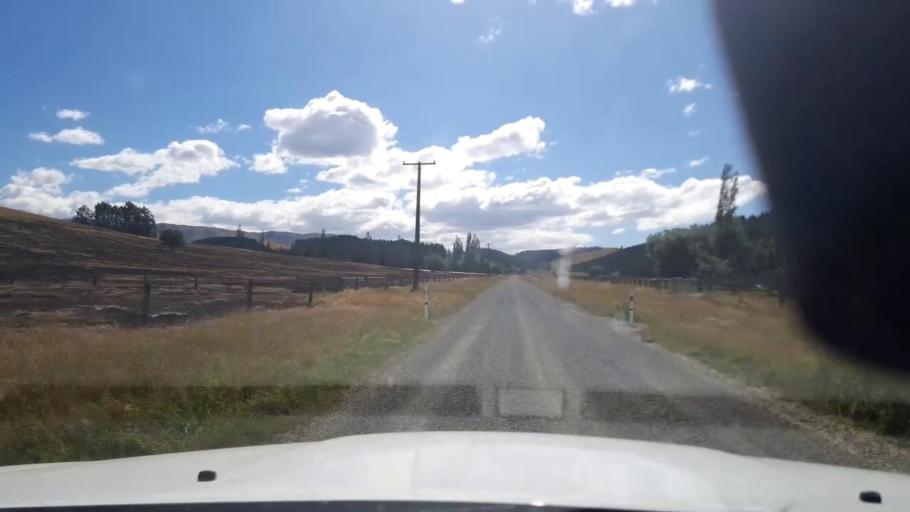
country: NZ
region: Canterbury
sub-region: Timaru District
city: Pleasant Point
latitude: -44.3150
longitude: 170.9279
